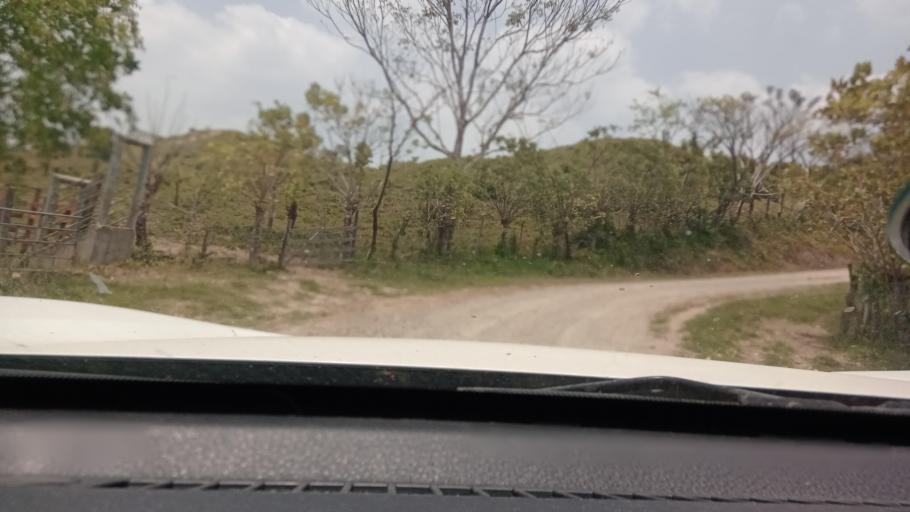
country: MX
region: Tabasco
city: Chontalpa
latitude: 17.5701
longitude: -93.7115
